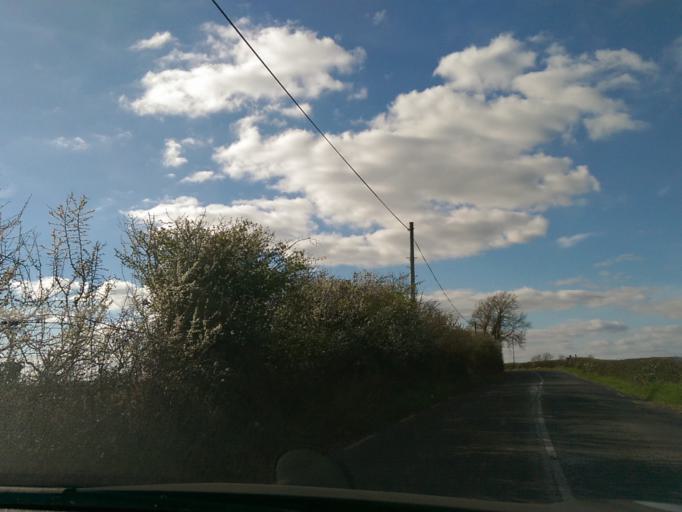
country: IE
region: Leinster
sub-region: Uibh Fhaili
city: Banagher
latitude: 53.1071
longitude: -8.0685
